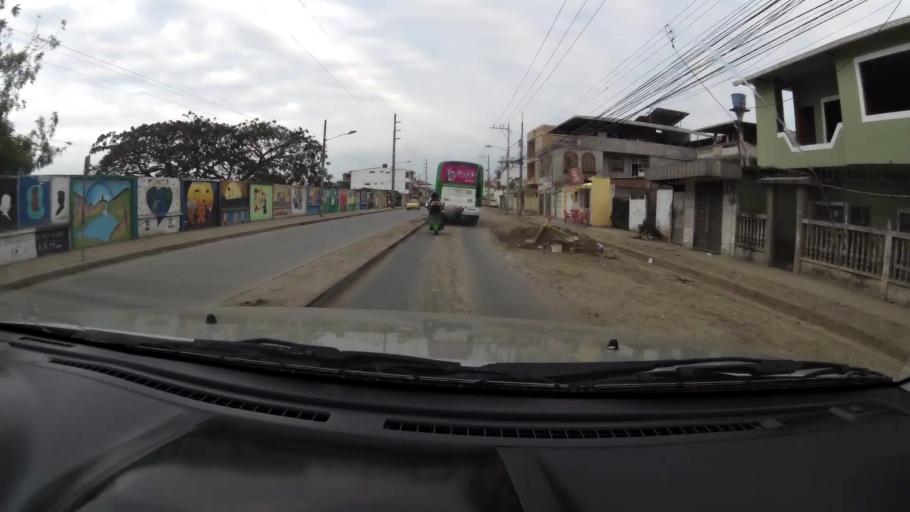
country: EC
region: El Oro
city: Machala
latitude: -3.2676
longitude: -79.9434
